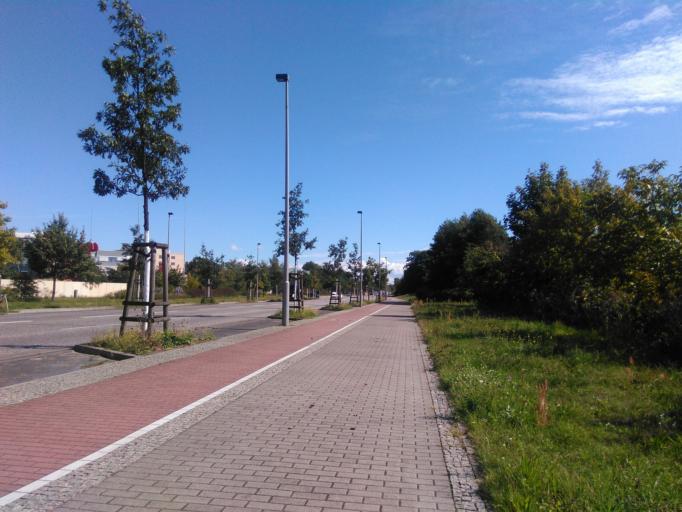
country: DE
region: Berlin
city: Altglienicke
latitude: 52.4259
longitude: 13.5334
